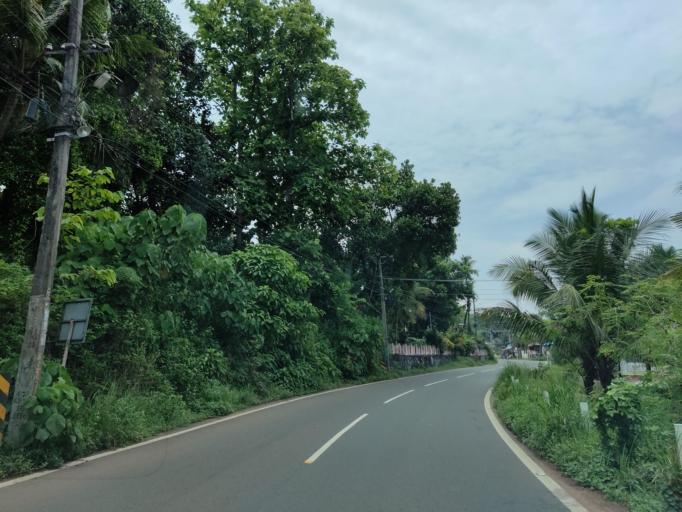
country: IN
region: Kerala
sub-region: Alappuzha
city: Chengannur
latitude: 9.2907
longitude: 76.6181
